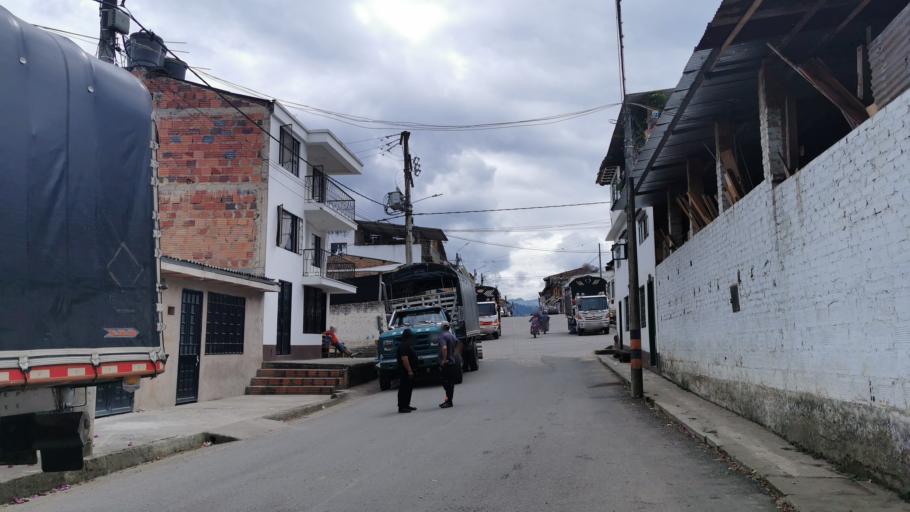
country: CO
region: Cundinamarca
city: Tenza
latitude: 5.0780
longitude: -73.4240
